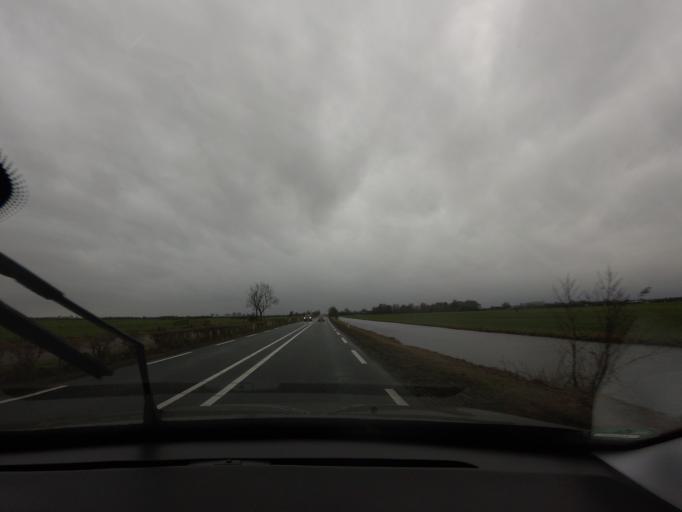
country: NL
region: Utrecht
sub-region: Stichtse Vecht
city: Breukelen
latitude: 52.1513
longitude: 4.9360
